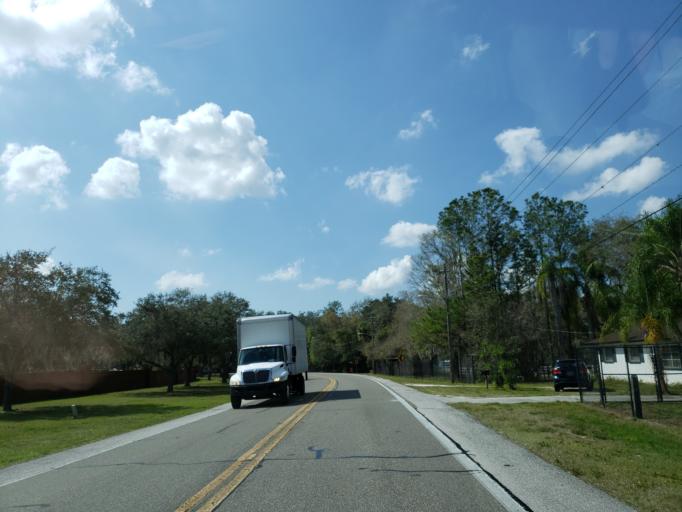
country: US
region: Florida
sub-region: Hillsborough County
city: Keystone
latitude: 28.1496
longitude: -82.5895
